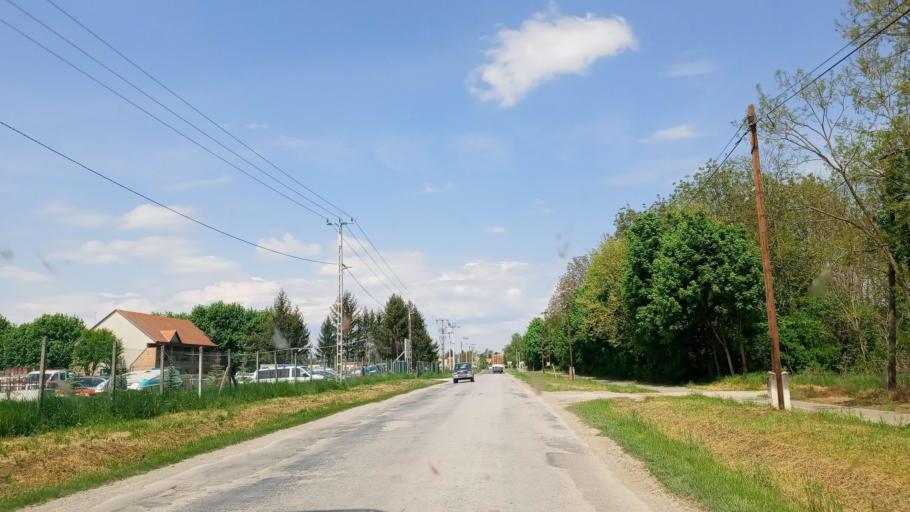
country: HU
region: Baranya
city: Boly
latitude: 45.9585
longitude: 18.5263
